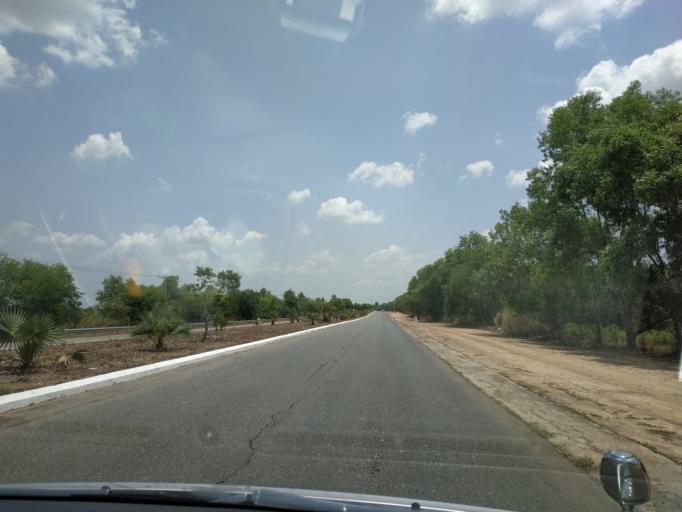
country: MM
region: Bago
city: Thanatpin
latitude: 17.1588
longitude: 96.1957
